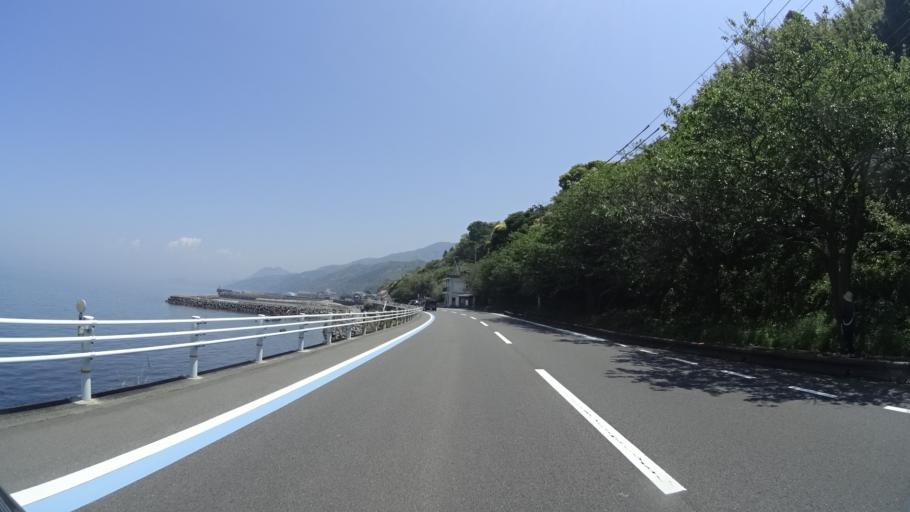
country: JP
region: Ehime
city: Ozu
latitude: 33.6489
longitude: 132.5685
